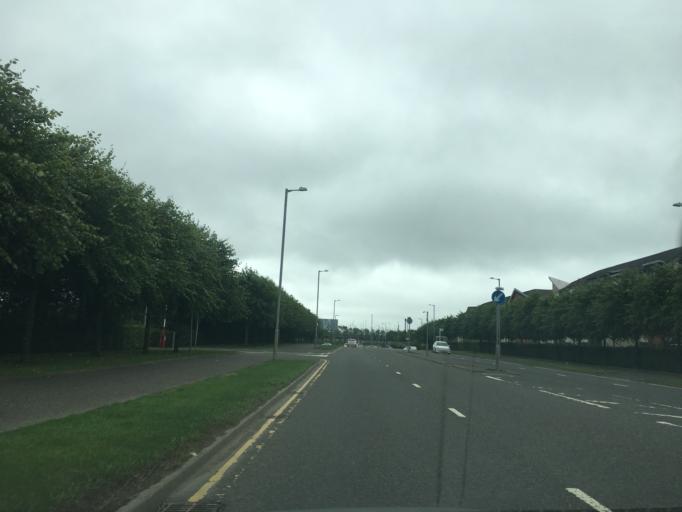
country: GB
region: Scotland
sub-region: Renfrewshire
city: Renfrew
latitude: 55.8777
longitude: -4.3726
